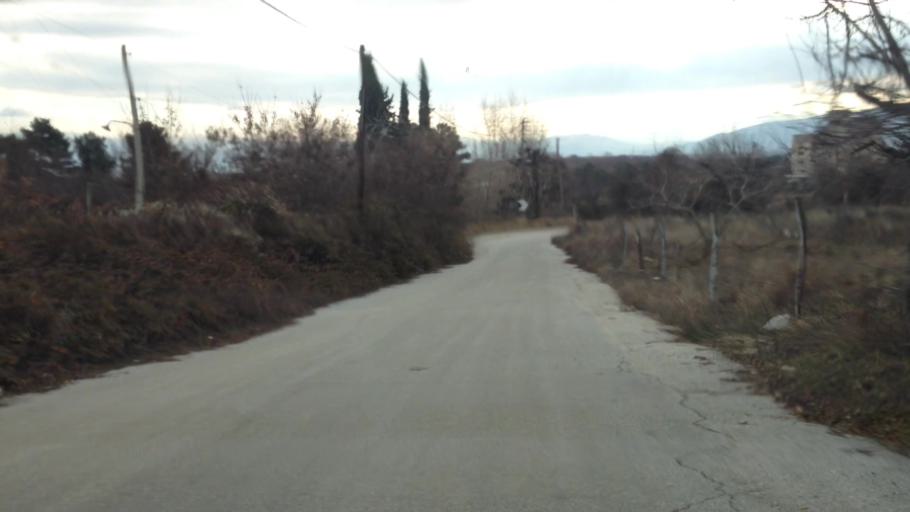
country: GR
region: West Macedonia
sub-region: Nomos Kozanis
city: Kozani
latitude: 40.2907
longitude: 21.7750
